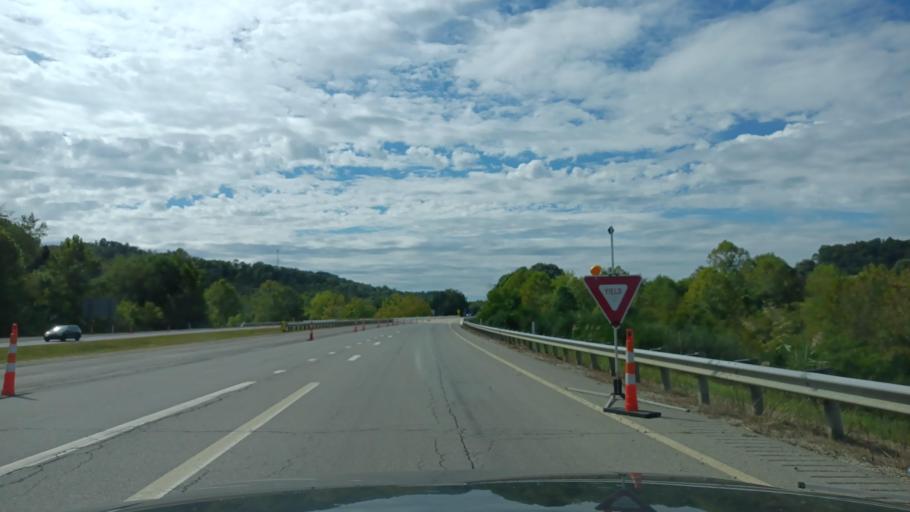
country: US
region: West Virginia
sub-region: Ritchie County
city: Harrisville
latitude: 39.2625
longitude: -81.0585
